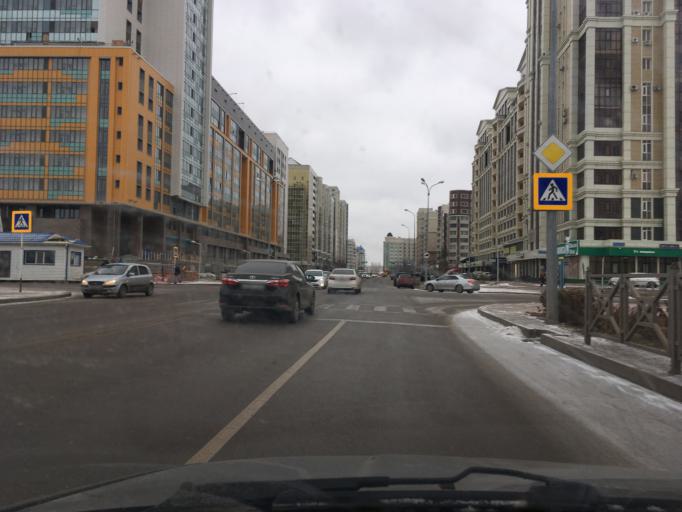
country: KZ
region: Astana Qalasy
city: Astana
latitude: 51.1162
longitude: 71.4271
